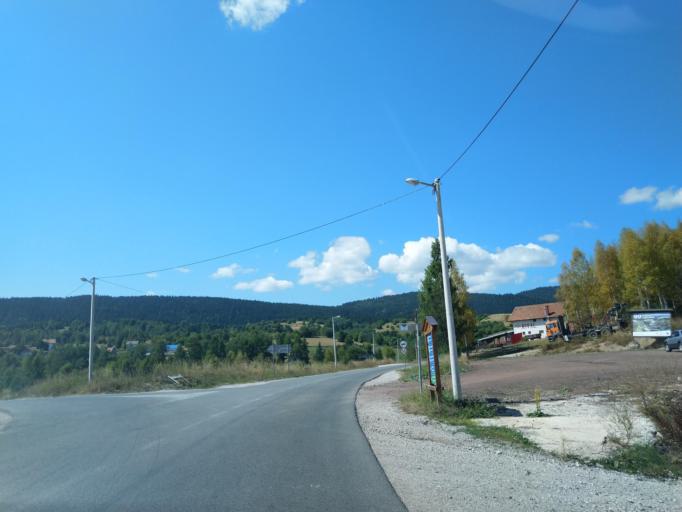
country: RS
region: Central Serbia
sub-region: Zlatiborski Okrug
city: Nova Varos
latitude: 43.4269
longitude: 19.8303
